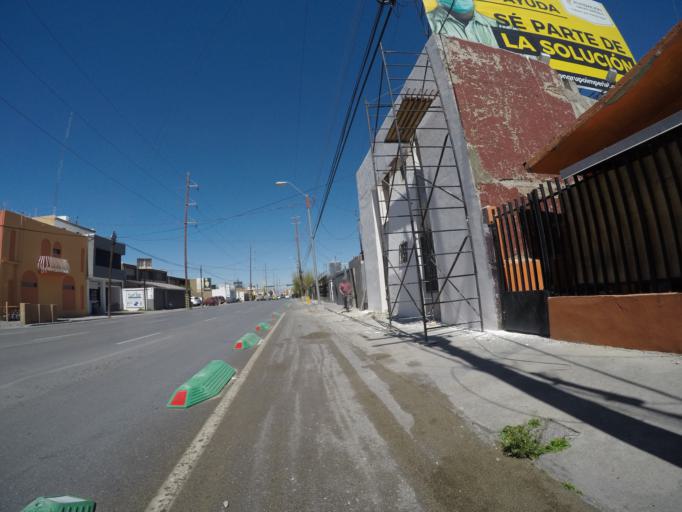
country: MX
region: Chihuahua
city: Ciudad Juarez
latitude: 31.7322
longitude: -106.4406
